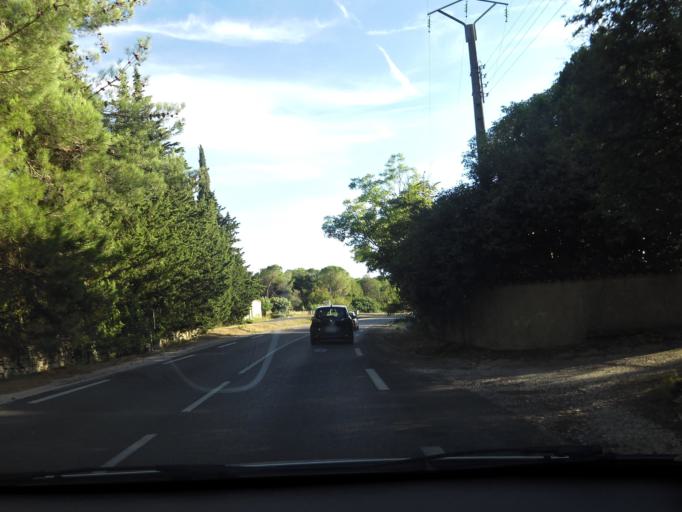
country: FR
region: Languedoc-Roussillon
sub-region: Departement de l'Herault
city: Saint-Mathieu-de-Treviers
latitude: 43.8079
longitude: 3.8870
